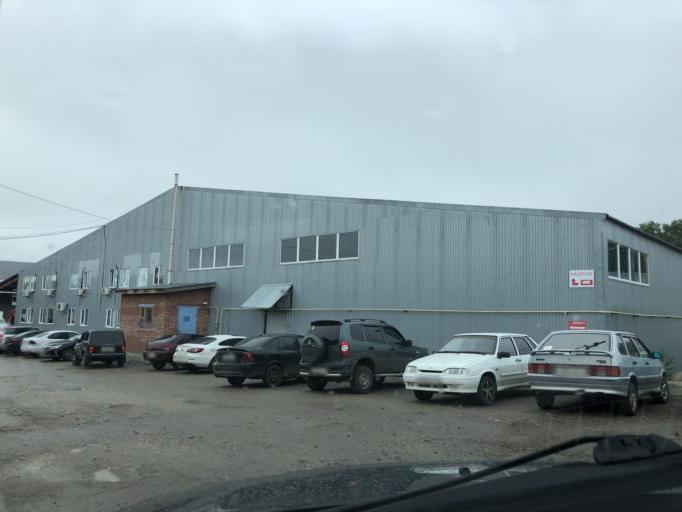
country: RU
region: Tula
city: Kosaya Gora
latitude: 54.1864
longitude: 37.5234
